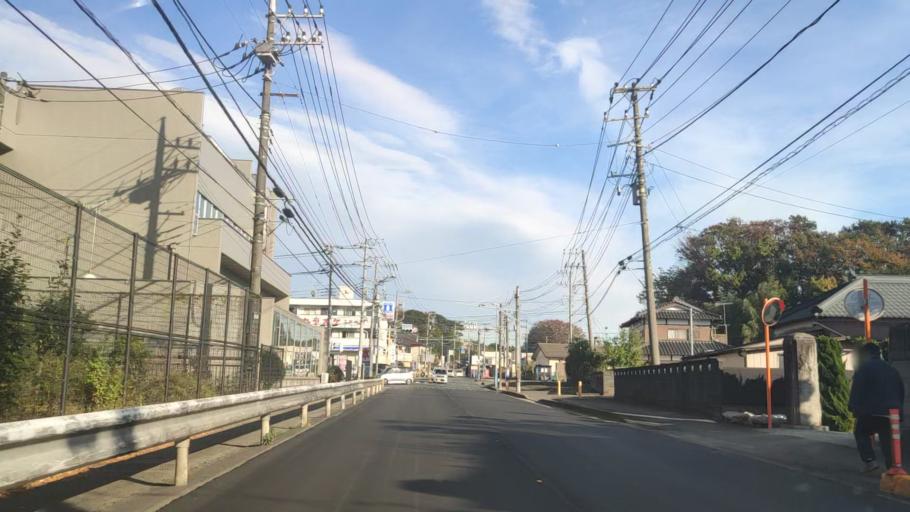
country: JP
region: Kanagawa
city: Atsugi
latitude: 35.4216
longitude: 139.3940
